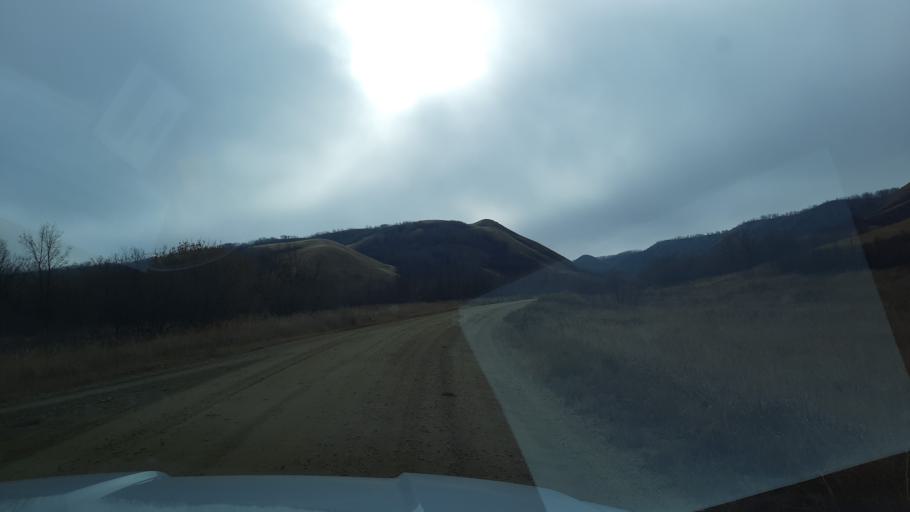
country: CA
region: Saskatchewan
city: White City
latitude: 50.7804
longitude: -104.1349
